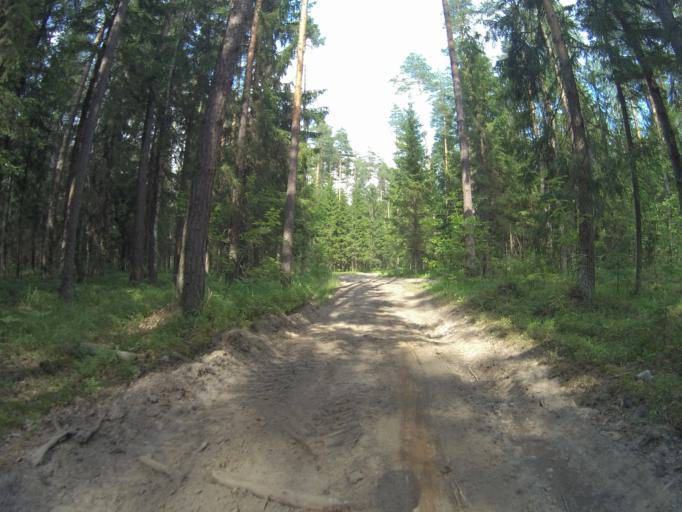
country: RU
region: Vladimir
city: Orgtrud
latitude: 56.1012
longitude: 40.5784
